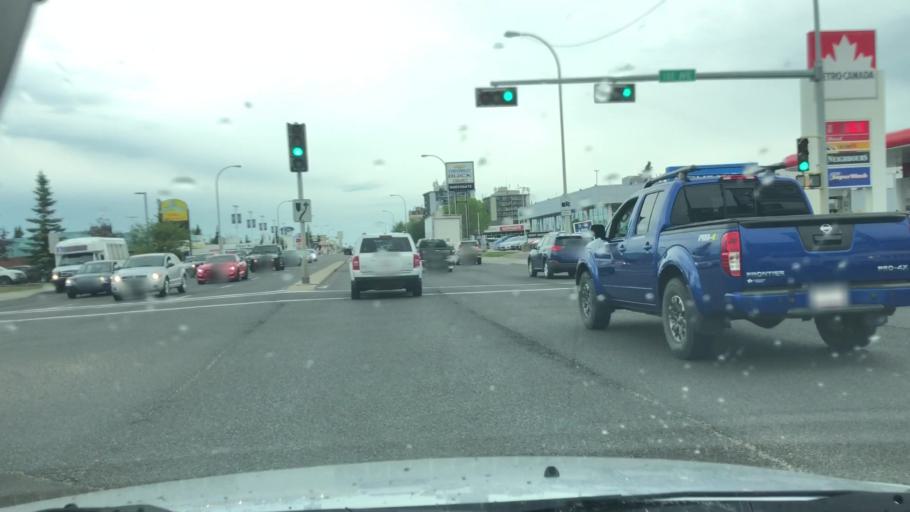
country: CA
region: Alberta
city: Edmonton
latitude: 53.5920
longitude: -113.4920
